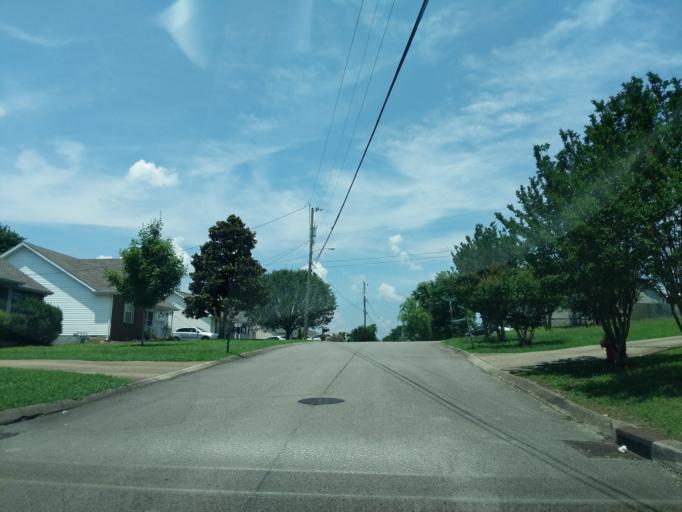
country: US
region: Tennessee
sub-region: Davidson County
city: Lakewood
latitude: 36.2396
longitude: -86.6359
